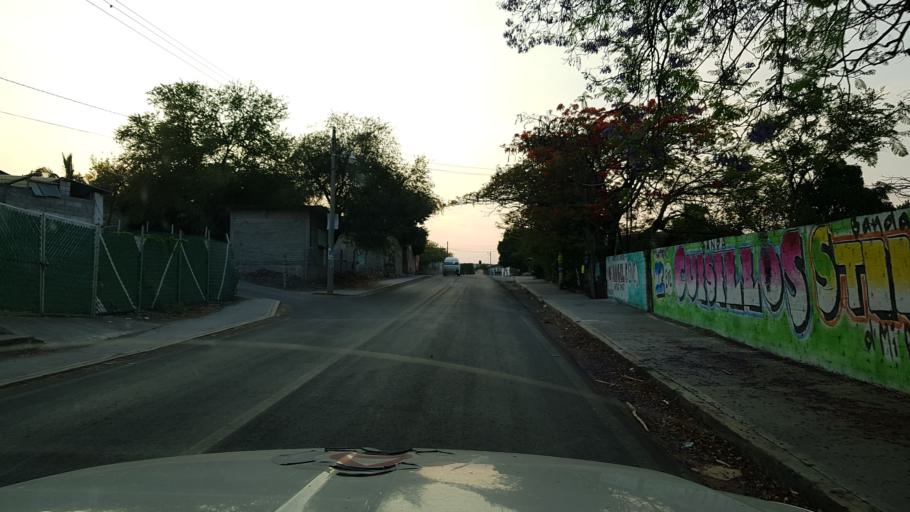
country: MX
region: Morelos
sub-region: Ayala
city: Abelardo L. Rodriguez
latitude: 18.7241
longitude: -98.9947
